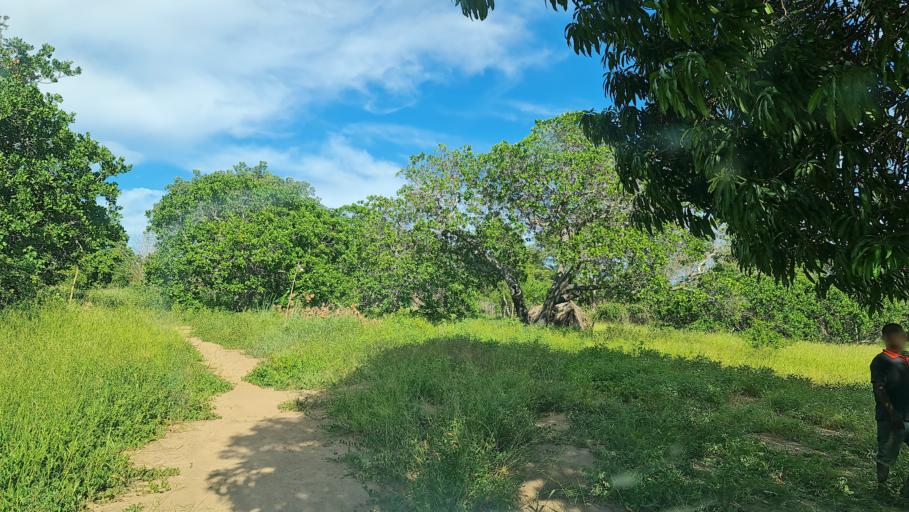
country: MZ
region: Nampula
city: Ilha de Mocambique
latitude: -15.5050
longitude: 40.1522
